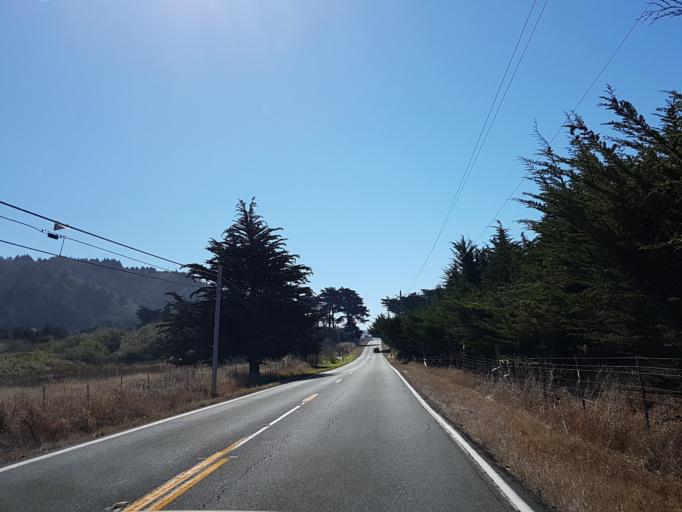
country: US
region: California
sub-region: Mendocino County
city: Boonville
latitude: 39.0905
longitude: -123.7014
